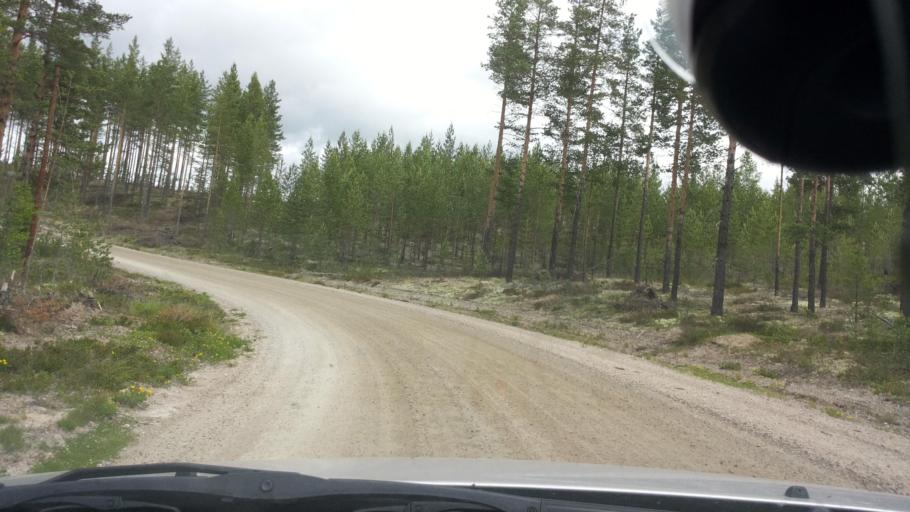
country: SE
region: Gaevleborg
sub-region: Ovanakers Kommun
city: Edsbyn
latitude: 61.5061
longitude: 15.3427
